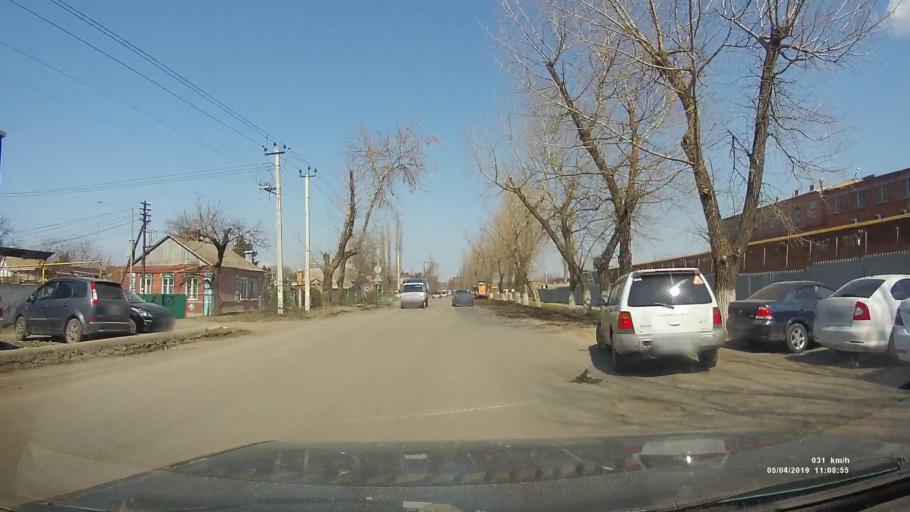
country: RU
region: Rostov
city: Azov
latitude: 47.0881
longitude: 39.4342
